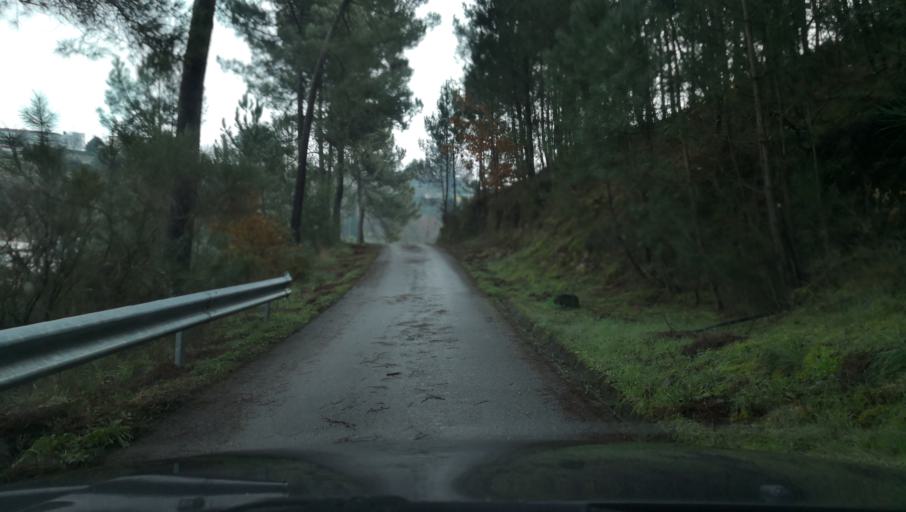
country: PT
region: Vila Real
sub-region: Vila Real
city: Vila Real
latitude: 41.2938
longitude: -7.7516
